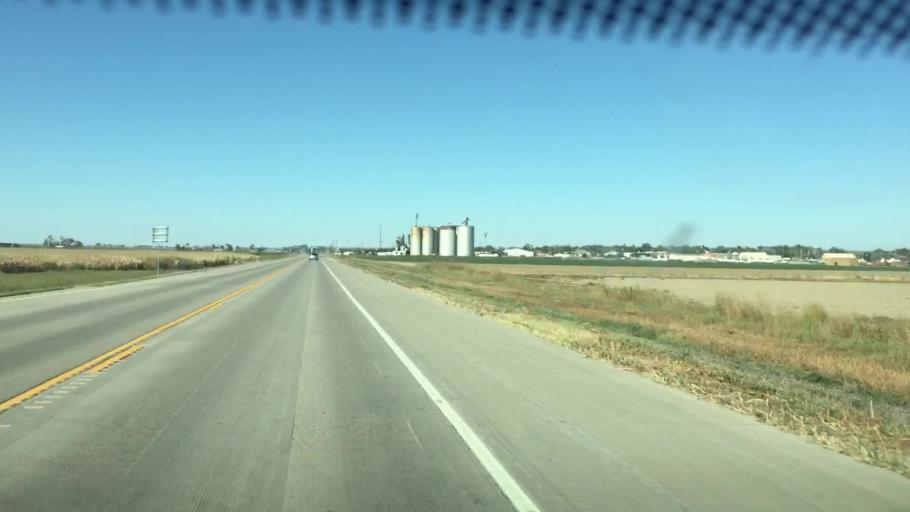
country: US
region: Colorado
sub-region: Prowers County
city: Lamar
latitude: 38.1452
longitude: -102.7238
